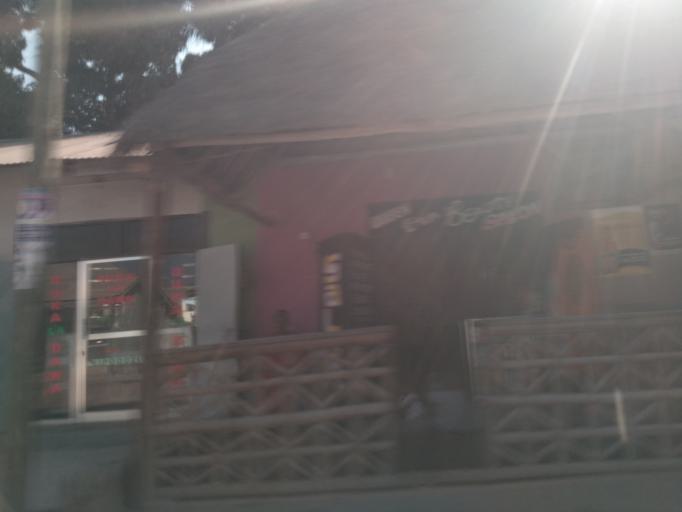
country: TZ
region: Dar es Salaam
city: Dar es Salaam
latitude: -6.8636
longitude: 39.3108
